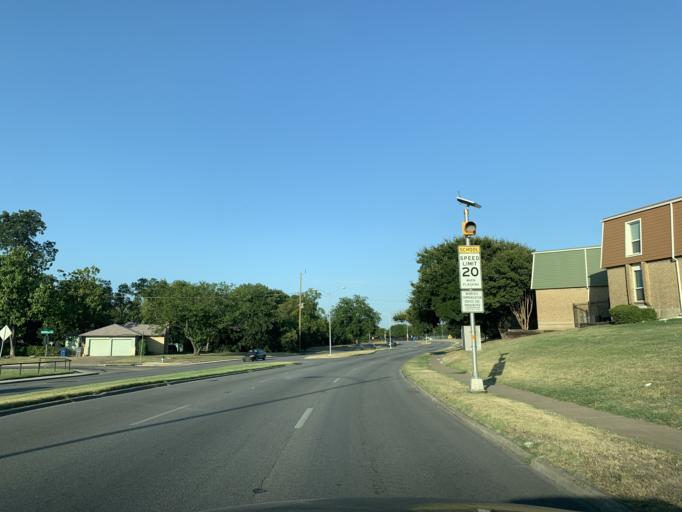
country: US
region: Texas
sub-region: Dallas County
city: Dallas
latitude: 32.7123
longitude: -96.7977
